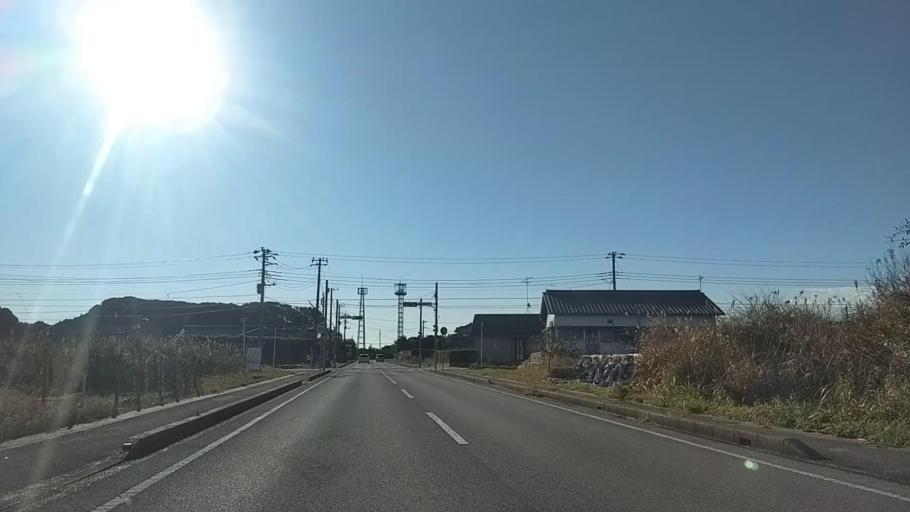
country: JP
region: Chiba
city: Futtsu
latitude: 35.3141
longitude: 139.8265
